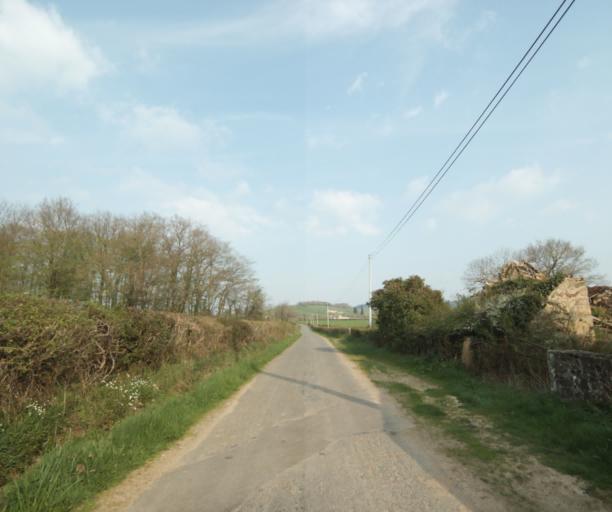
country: FR
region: Bourgogne
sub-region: Departement de Saone-et-Loire
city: Matour
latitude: 46.4601
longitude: 4.4418
